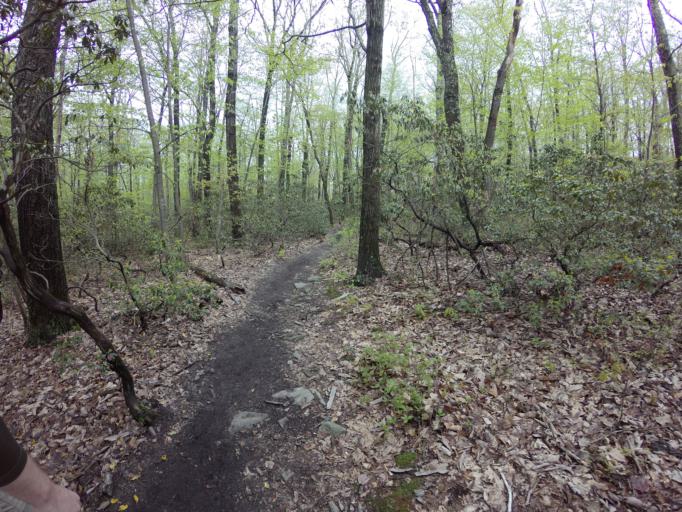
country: US
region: Maryland
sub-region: Washington County
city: Boonsboro
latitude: 39.5235
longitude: -77.6155
